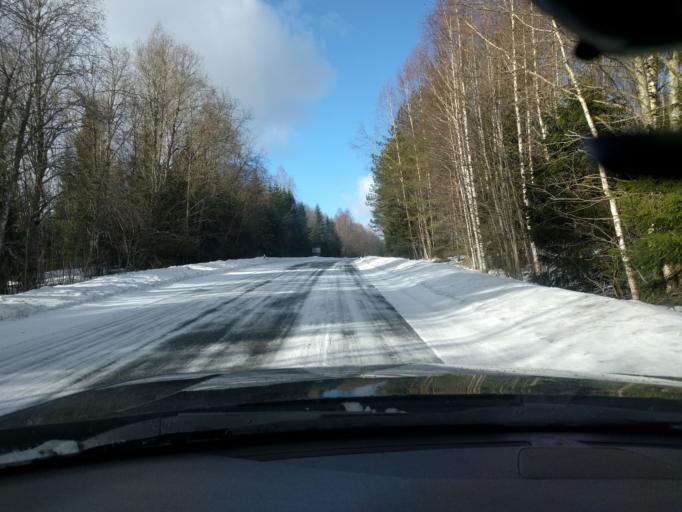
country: EE
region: Harju
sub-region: Anija vald
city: Kehra
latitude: 59.2116
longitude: 25.5083
